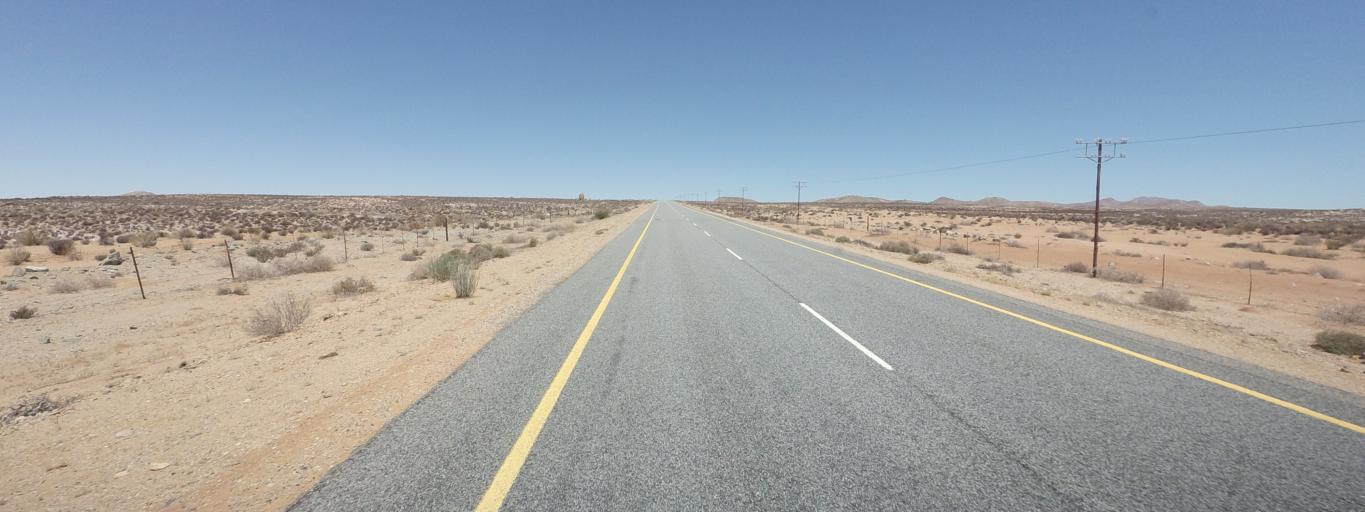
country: ZA
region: Northern Cape
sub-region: Namakwa District Municipality
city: Springbok
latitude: -29.0701
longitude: 17.8498
